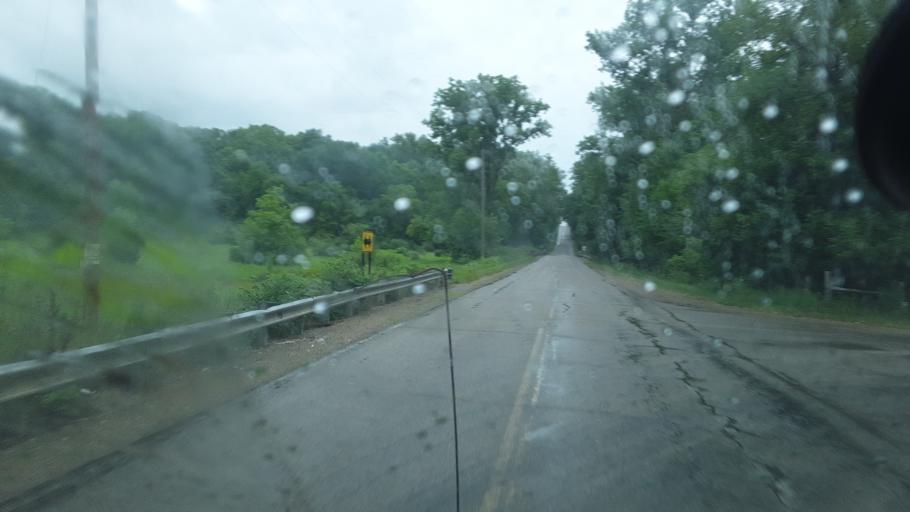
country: US
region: Ohio
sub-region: Williams County
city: Pioneer
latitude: 41.7085
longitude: -84.6895
